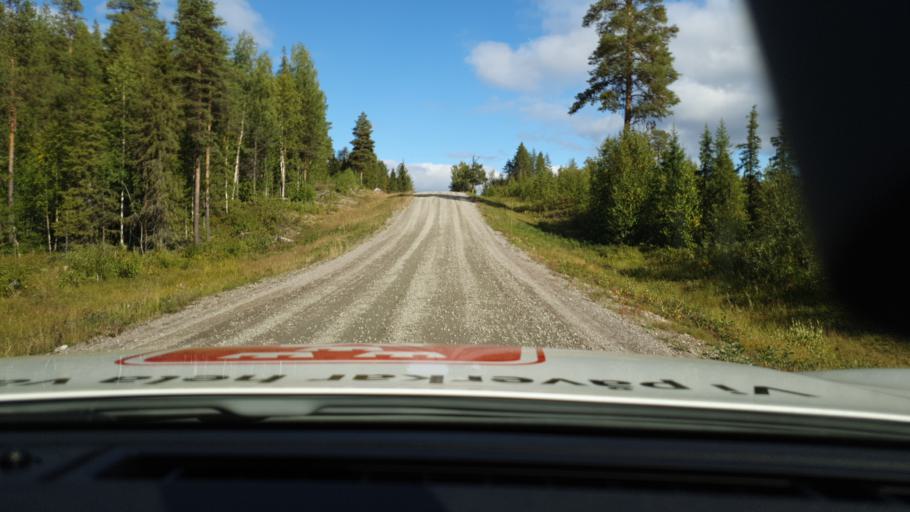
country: SE
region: Norrbotten
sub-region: Pajala Kommun
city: Pajala
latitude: 67.3871
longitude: 22.4359
